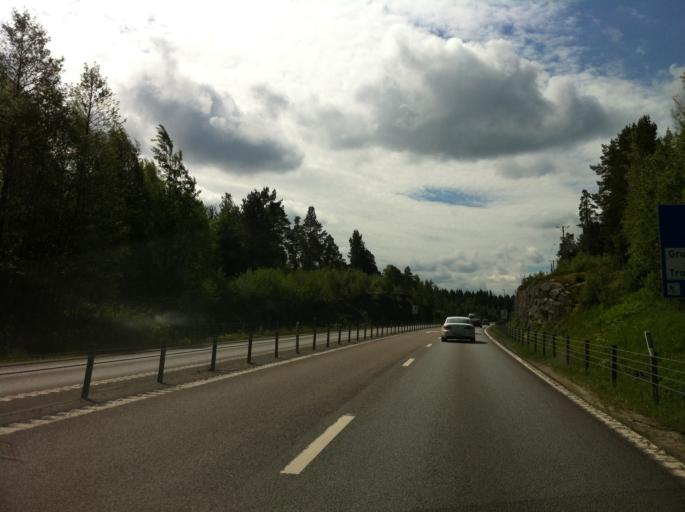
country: SE
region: Vaermland
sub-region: Grums Kommun
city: Grums
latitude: 59.3575
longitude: 13.1319
